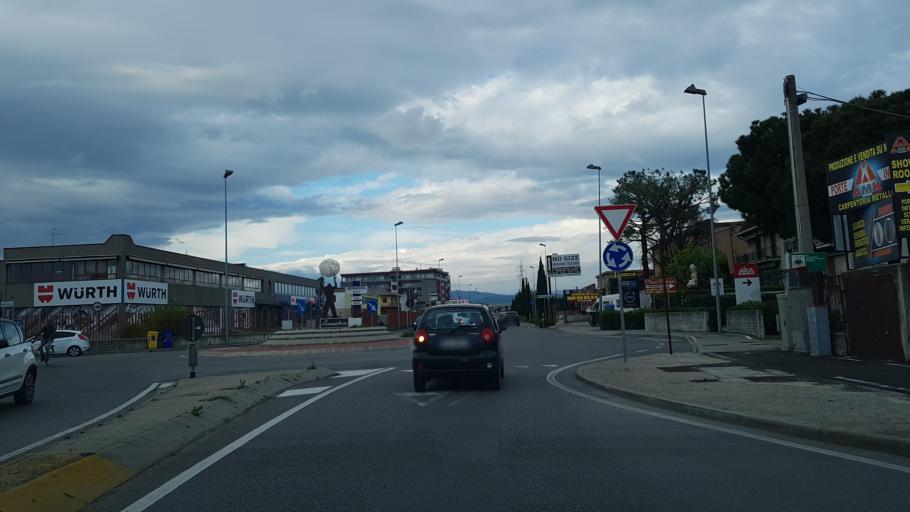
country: IT
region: Veneto
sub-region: Provincia di Verona
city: San Giovanni Lupatoto
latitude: 45.3935
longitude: 11.0212
